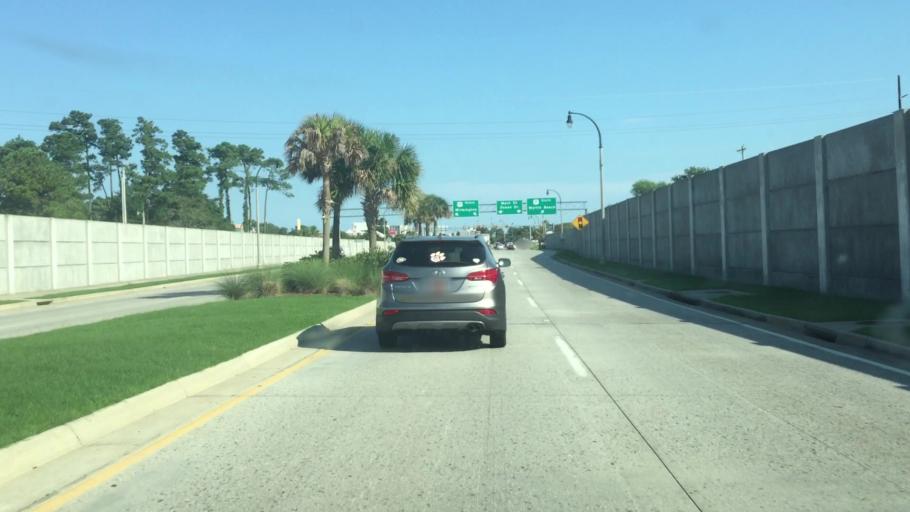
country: US
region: South Carolina
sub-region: Horry County
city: North Myrtle Beach
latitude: 33.8308
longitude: -78.6819
